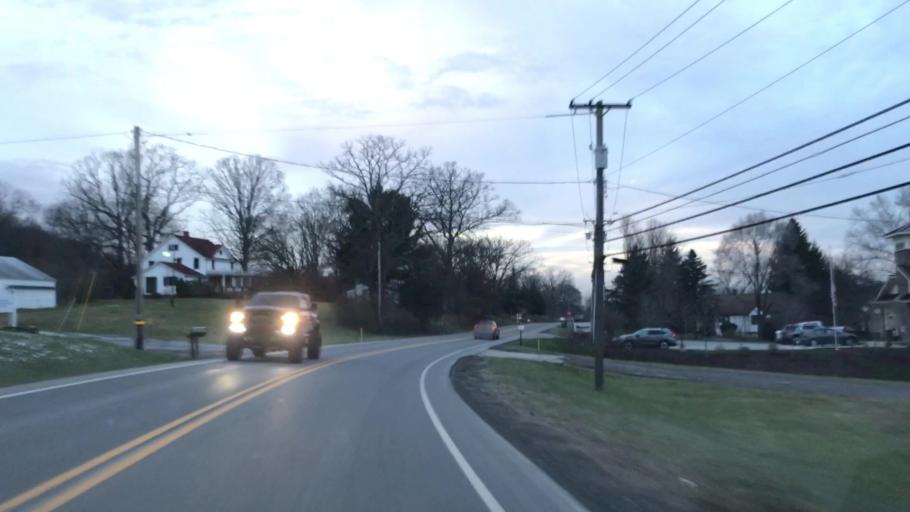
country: US
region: Pennsylvania
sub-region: Butler County
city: Mars
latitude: 40.6848
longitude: -80.0039
